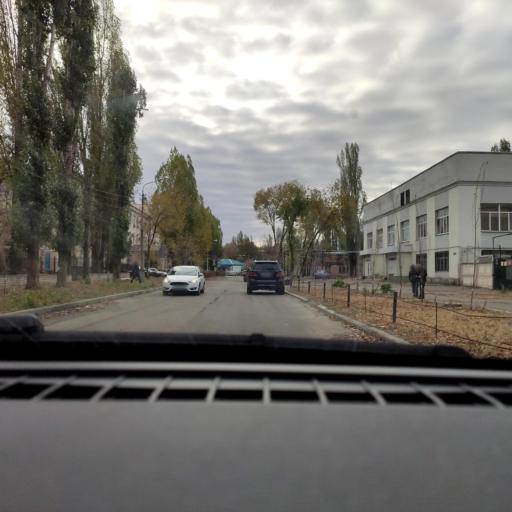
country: RU
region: Voronezj
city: Voronezh
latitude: 51.6312
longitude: 39.2367
